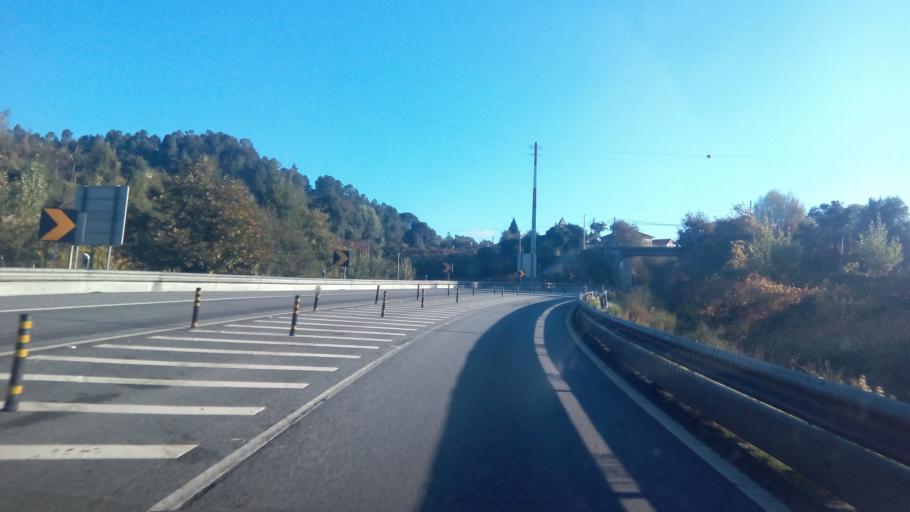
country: PT
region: Porto
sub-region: Amarante
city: Amarante
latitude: 41.2747
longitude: -8.0082
